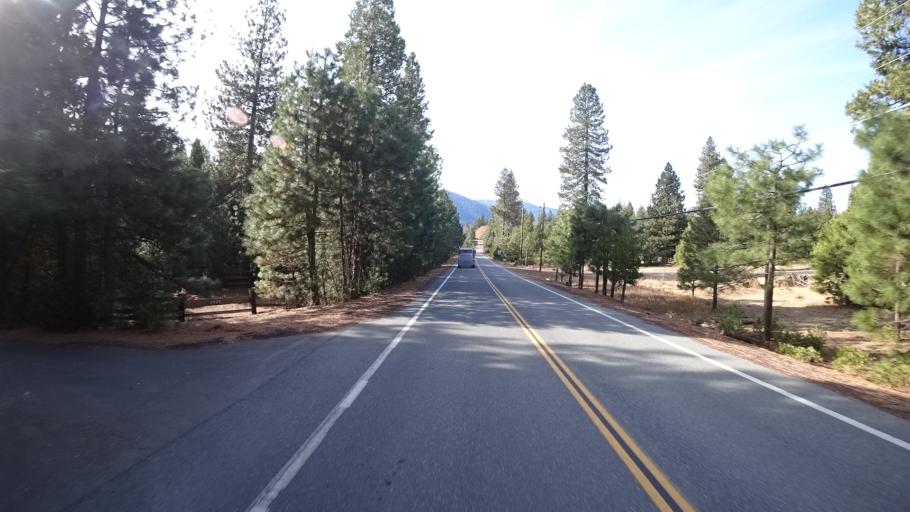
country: US
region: California
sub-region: Siskiyou County
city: Weed
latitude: 41.3834
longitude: -122.4011
